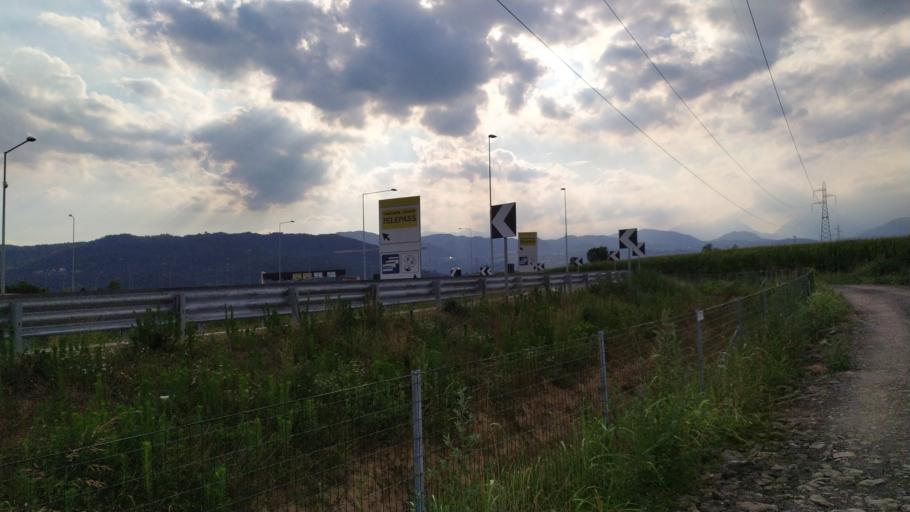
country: IT
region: Veneto
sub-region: Provincia di Vicenza
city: Isola Vicentina
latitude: 45.6498
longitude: 11.4474
